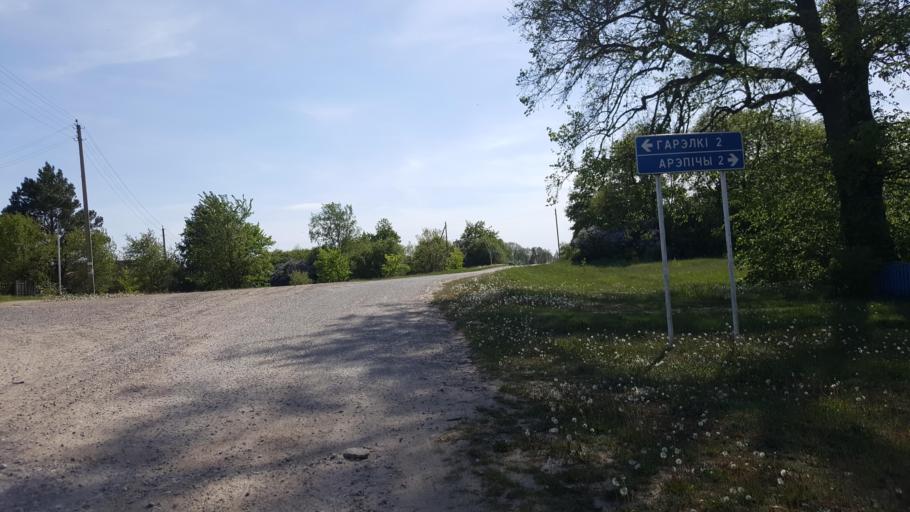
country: BY
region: Brest
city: Zhabinka
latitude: 52.3159
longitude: 24.0409
